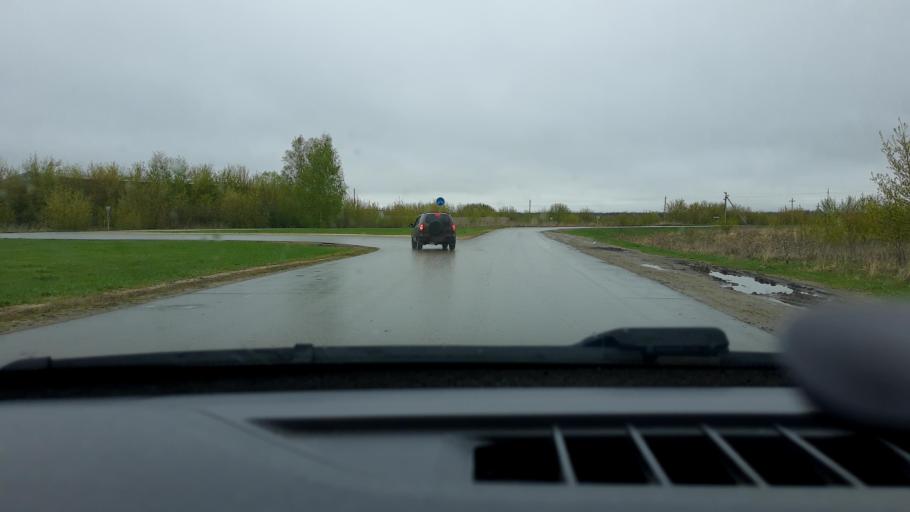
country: RU
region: Nizjnij Novgorod
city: Buturlino
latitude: 55.5720
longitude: 44.8563
